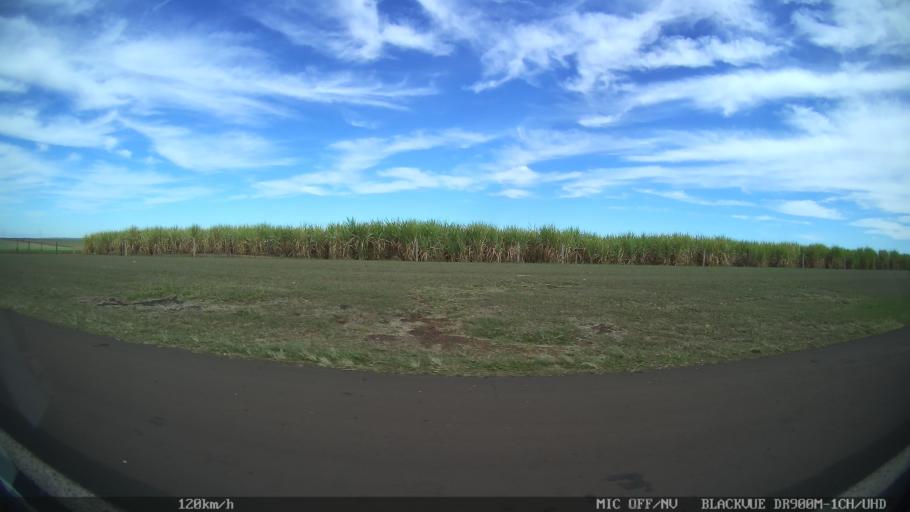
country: BR
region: Sao Paulo
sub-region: Taquaritinga
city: Taquaritinga
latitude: -21.4878
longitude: -48.5812
